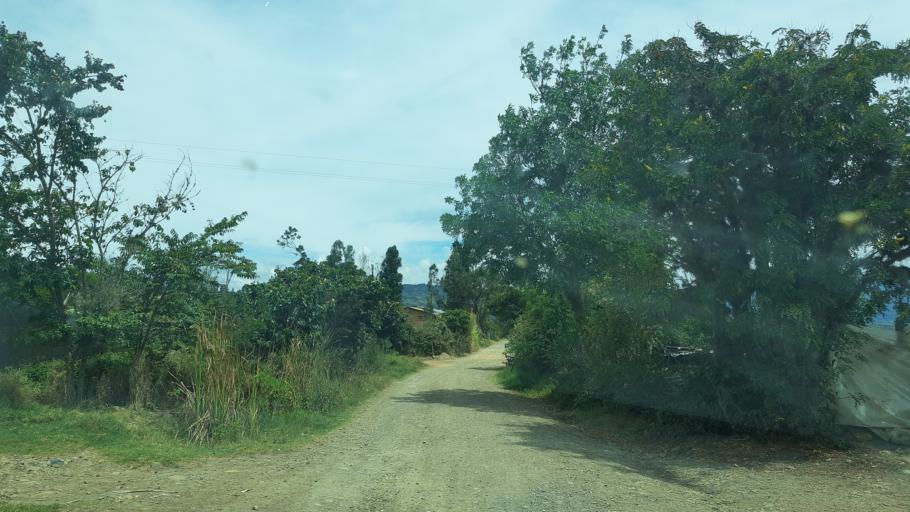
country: CO
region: Boyaca
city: Santa Sofia
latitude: 5.6825
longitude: -73.5927
